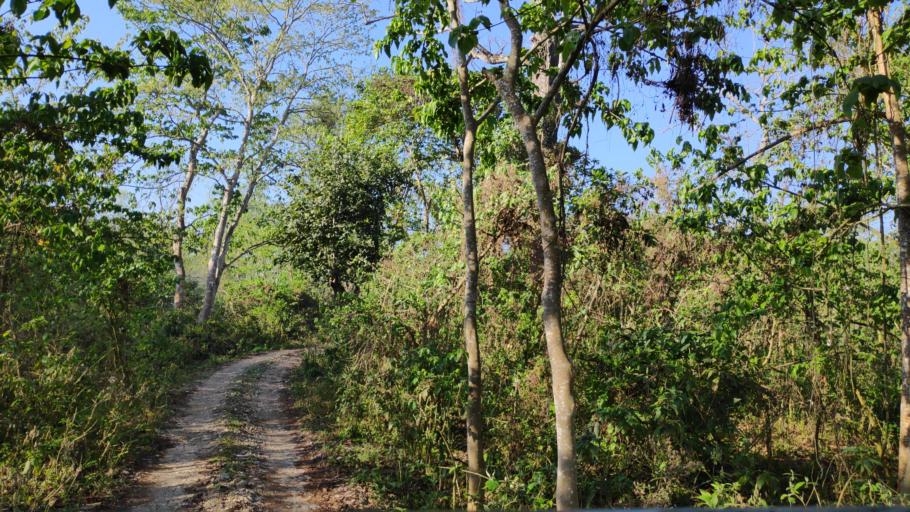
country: NP
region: Central Region
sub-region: Narayani Zone
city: Bharatpur
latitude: 27.5577
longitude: 84.5570
